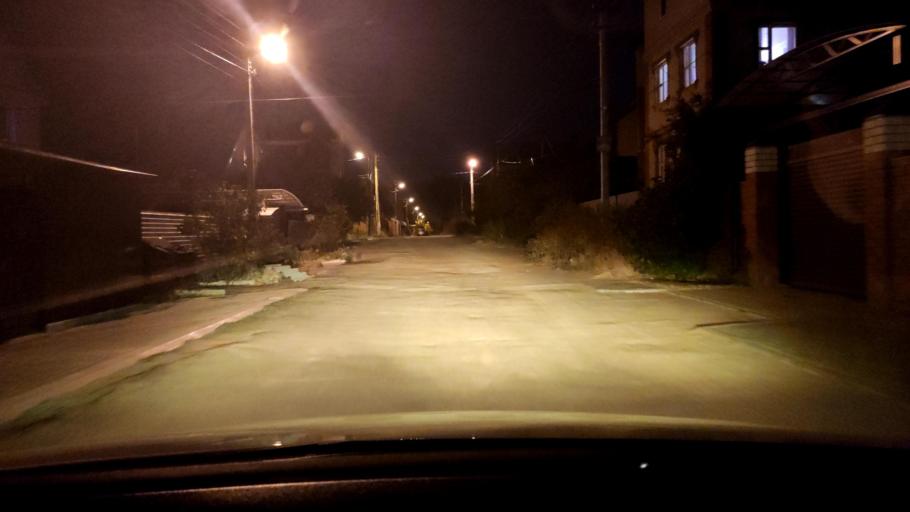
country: RU
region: Voronezj
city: Pridonskoy
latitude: 51.6535
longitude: 39.0989
